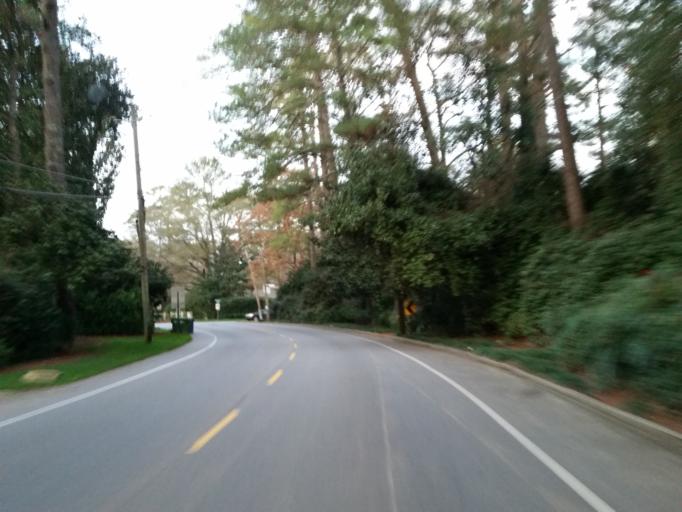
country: US
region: Georgia
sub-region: Cobb County
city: Vinings
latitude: 33.8591
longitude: -84.4035
